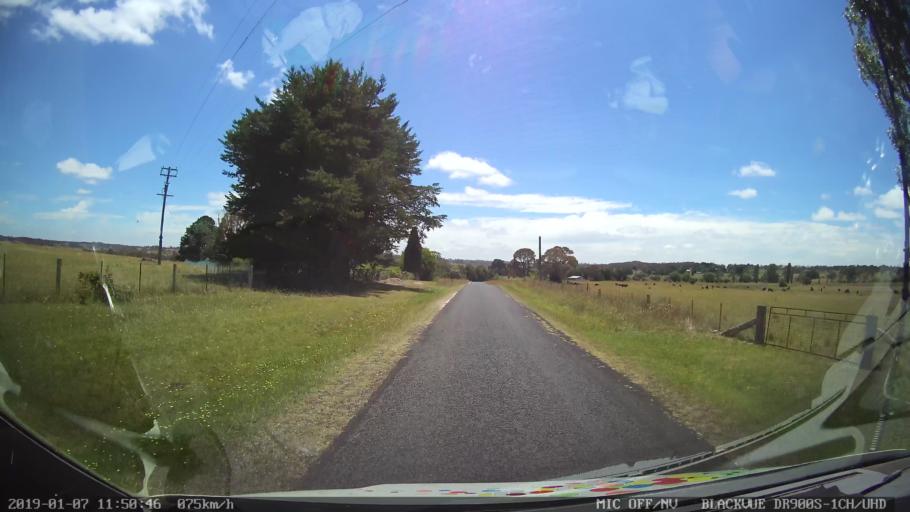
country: AU
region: New South Wales
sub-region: Guyra
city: Guyra
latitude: -30.3111
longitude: 151.6394
